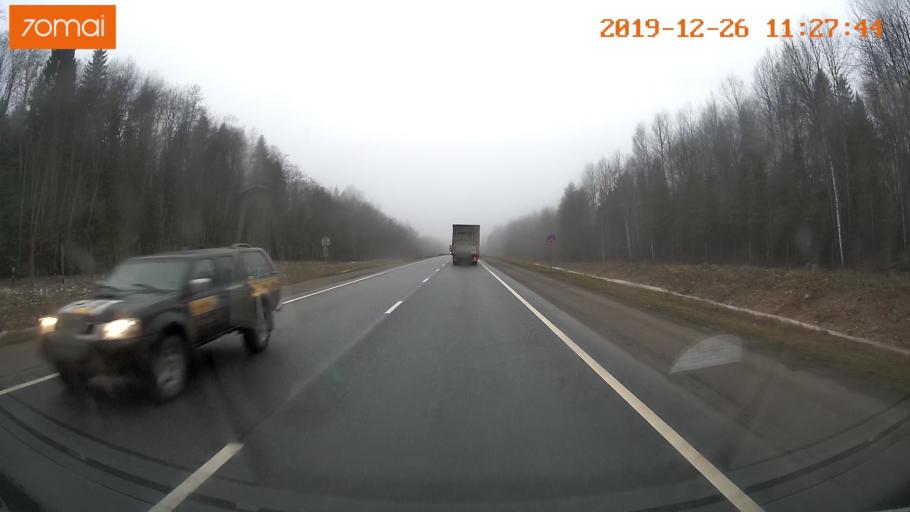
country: RU
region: Vologda
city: Chebsara
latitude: 59.1525
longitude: 38.8297
